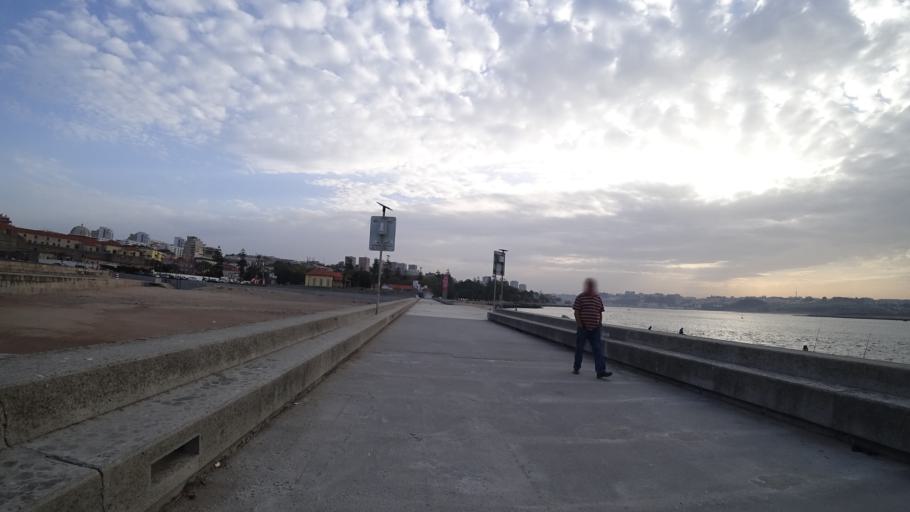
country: PT
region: Porto
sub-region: Vila Nova de Gaia
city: Canidelo
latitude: 41.1473
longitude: -8.6761
